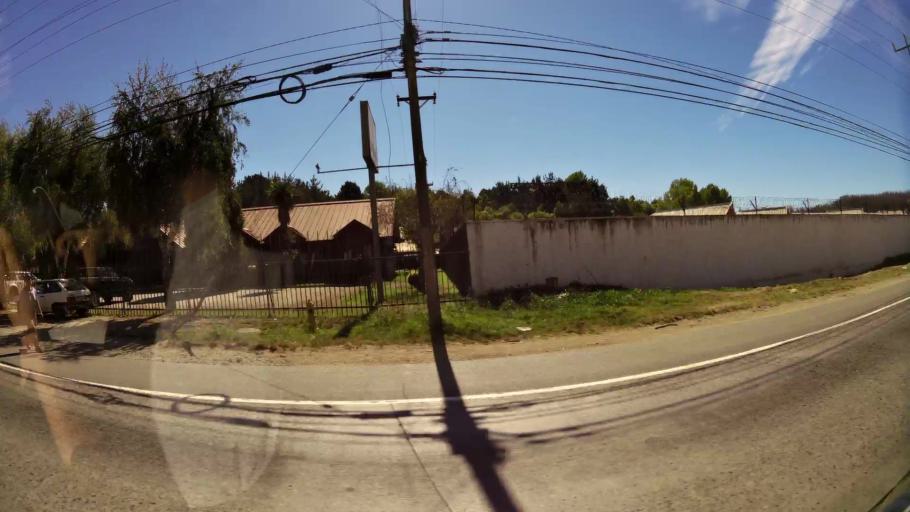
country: CL
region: Biobio
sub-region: Provincia de Concepcion
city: Penco
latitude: -36.7730
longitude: -73.0154
